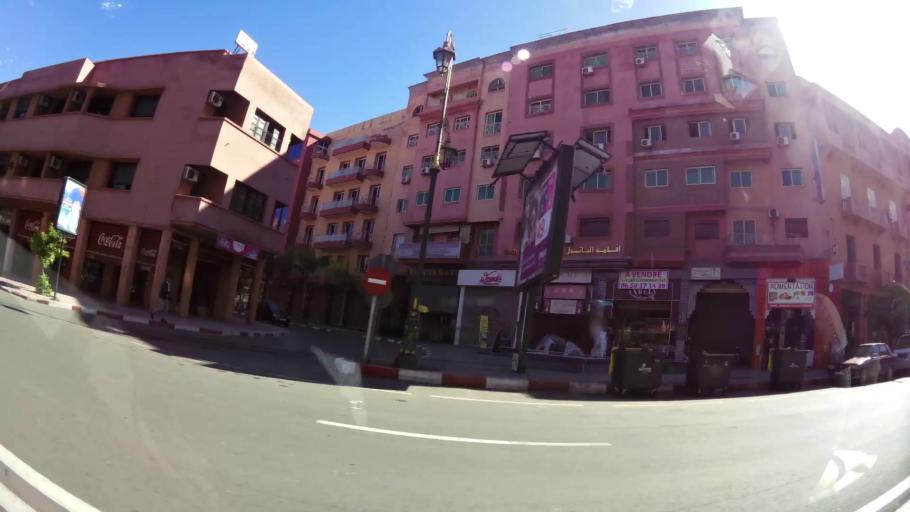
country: MA
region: Marrakech-Tensift-Al Haouz
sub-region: Marrakech
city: Marrakesh
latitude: 31.6371
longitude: -8.0163
